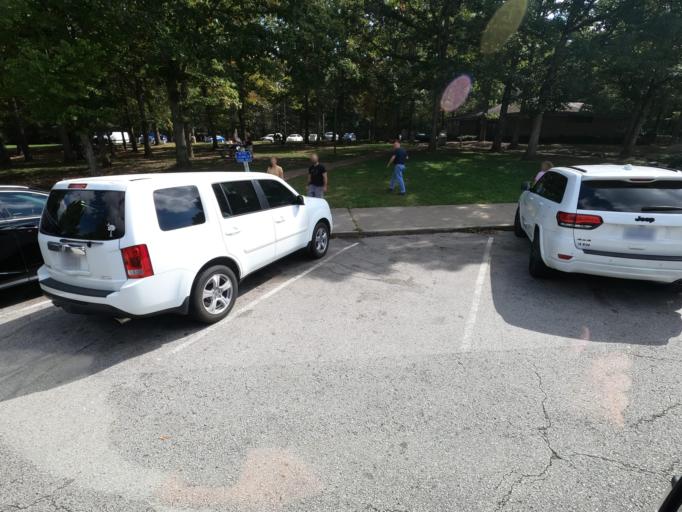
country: US
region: Tennessee
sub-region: Cumberland County
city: Fairfield Glade
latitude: 35.9468
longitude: -84.9445
